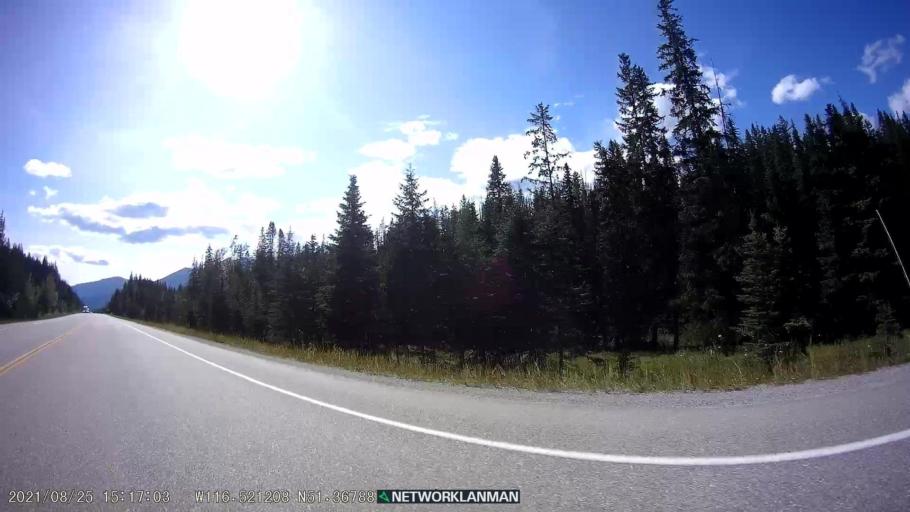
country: CA
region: Alberta
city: Lake Louise
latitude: 51.3680
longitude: -116.5215
